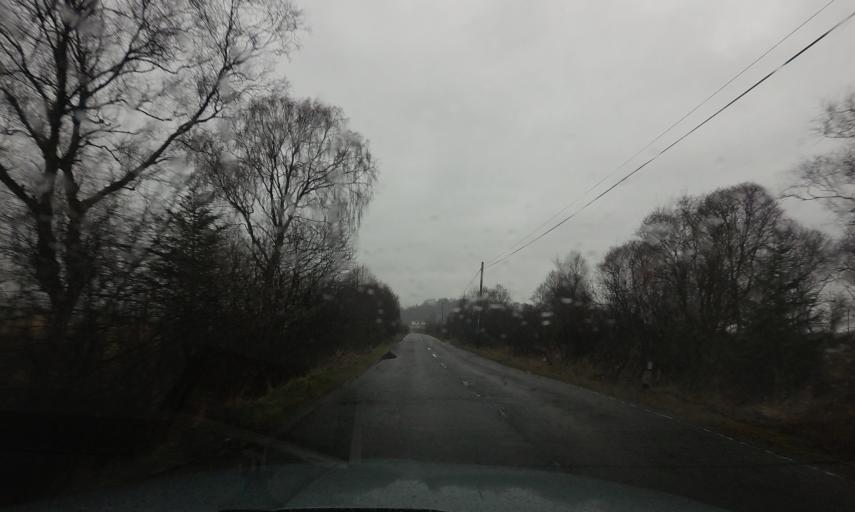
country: GB
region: Scotland
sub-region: Stirling
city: Balfron
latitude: 56.1325
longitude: -4.3582
